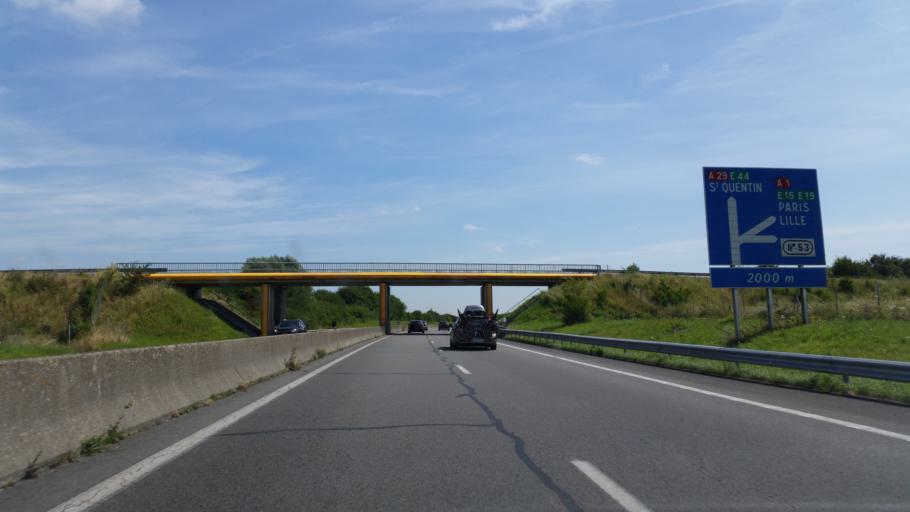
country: FR
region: Picardie
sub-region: Departement de la Somme
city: Chaulnes
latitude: 49.8580
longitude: 2.7801
